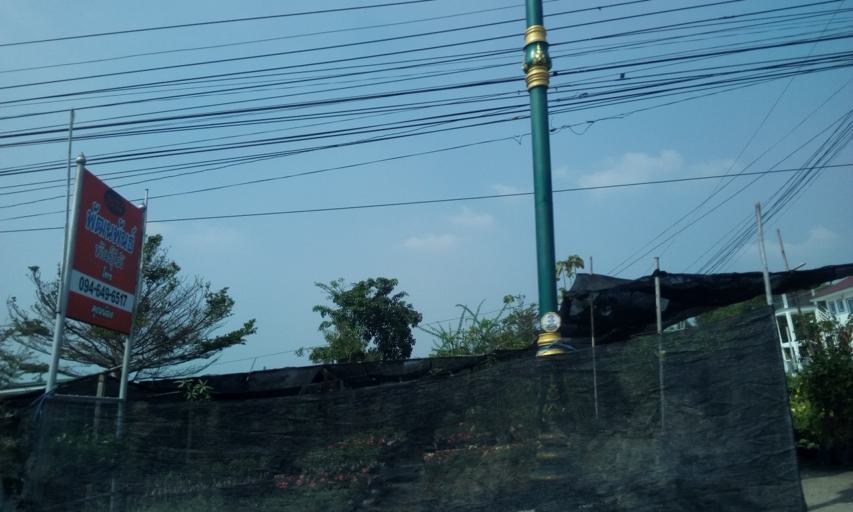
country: TH
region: Nakhon Nayok
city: Ongkharak
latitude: 14.1281
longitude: 100.9466
